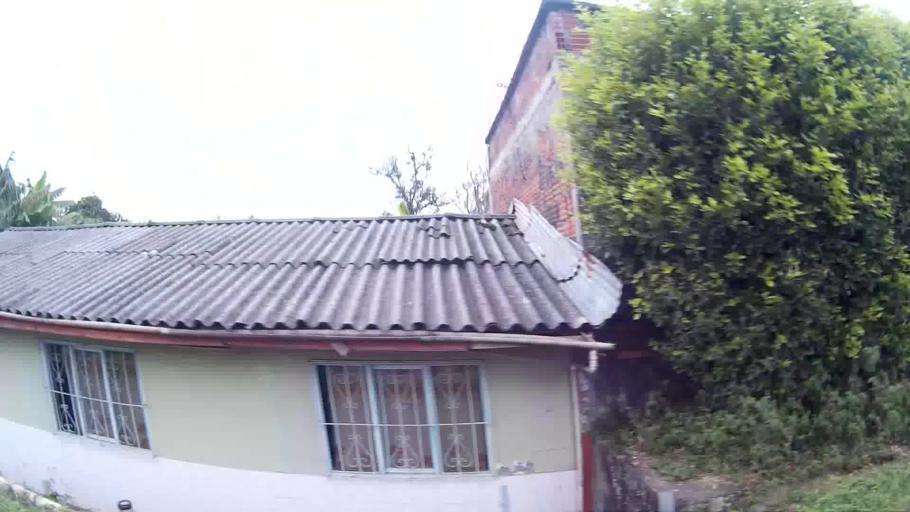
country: CO
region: Risaralda
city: Pereira
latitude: 4.7894
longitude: -75.7324
